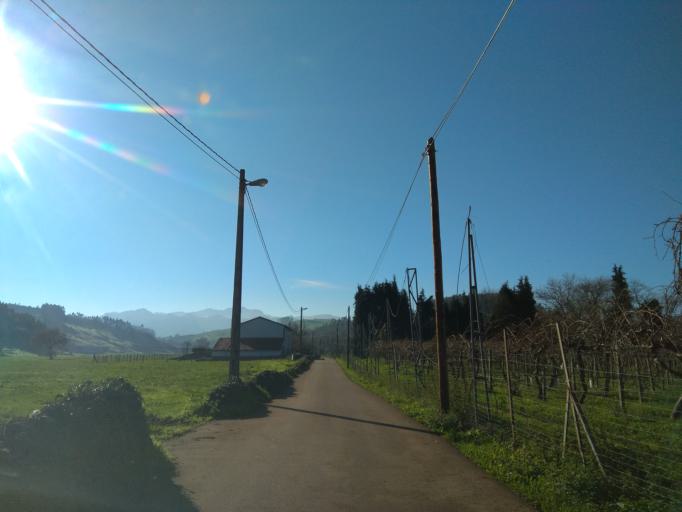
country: ES
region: Cantabria
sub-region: Provincia de Cantabria
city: Entrambasaguas
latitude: 43.3731
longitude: -3.7101
